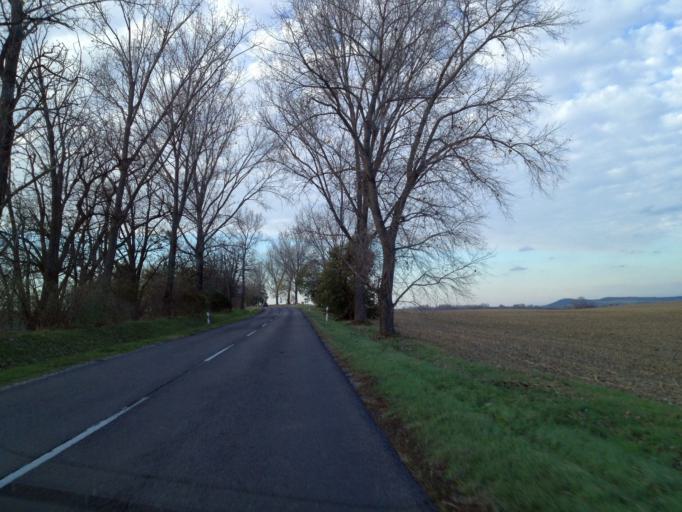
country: HU
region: Gyor-Moson-Sopron
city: Bakonyszentlaszlo
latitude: 47.4526
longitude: 17.8106
